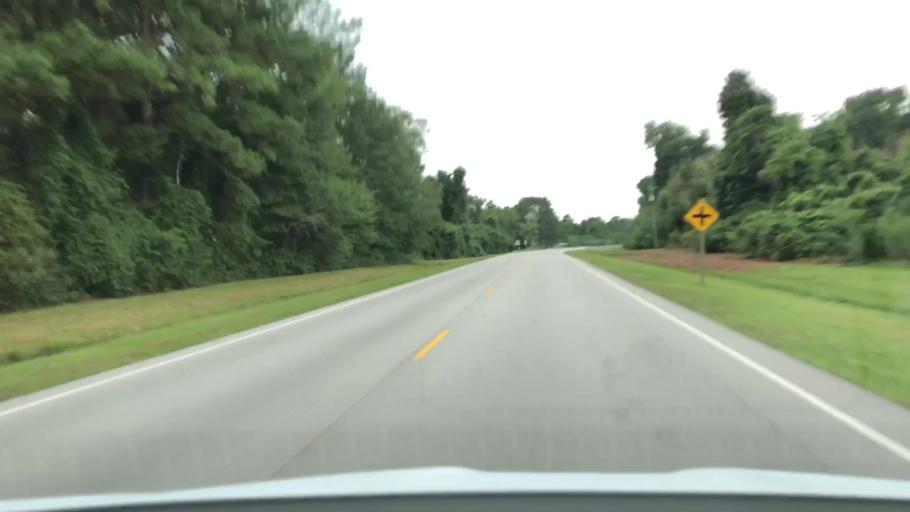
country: US
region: North Carolina
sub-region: Jones County
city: Trenton
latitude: 35.0173
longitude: -77.2993
